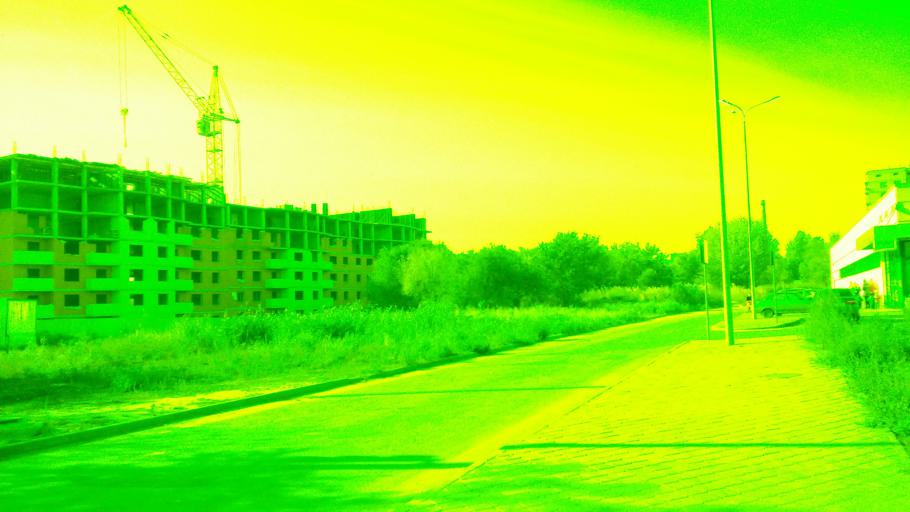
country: RU
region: Volgograd
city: Vodstroy
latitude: 48.8385
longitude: 44.6463
